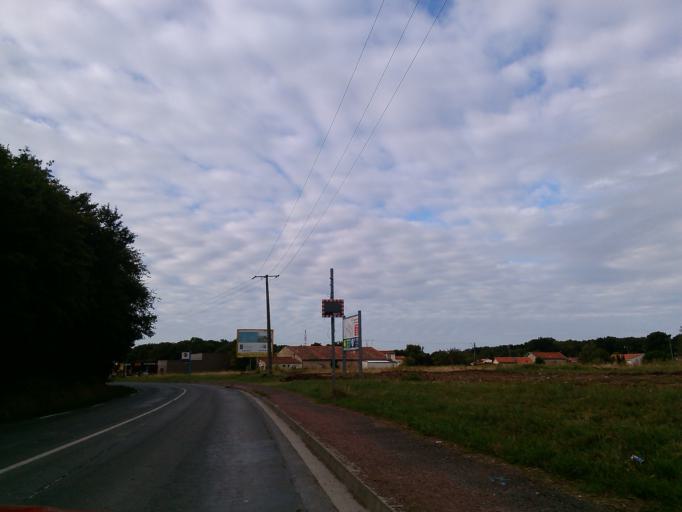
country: FR
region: Poitou-Charentes
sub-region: Departement de la Charente-Maritime
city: Royan
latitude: 45.6506
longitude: -1.0245
